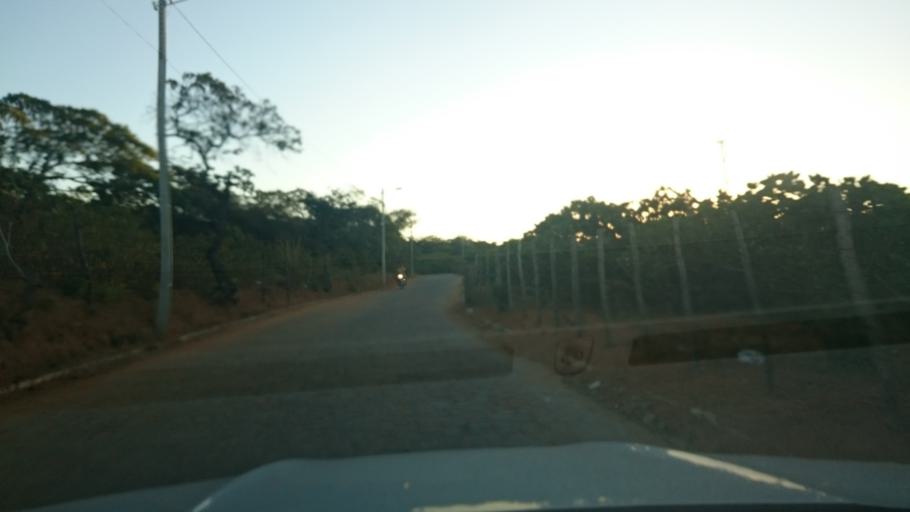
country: BR
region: Rio Grande do Norte
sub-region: Umarizal
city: Umarizal
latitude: -6.0221
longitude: -37.9951
